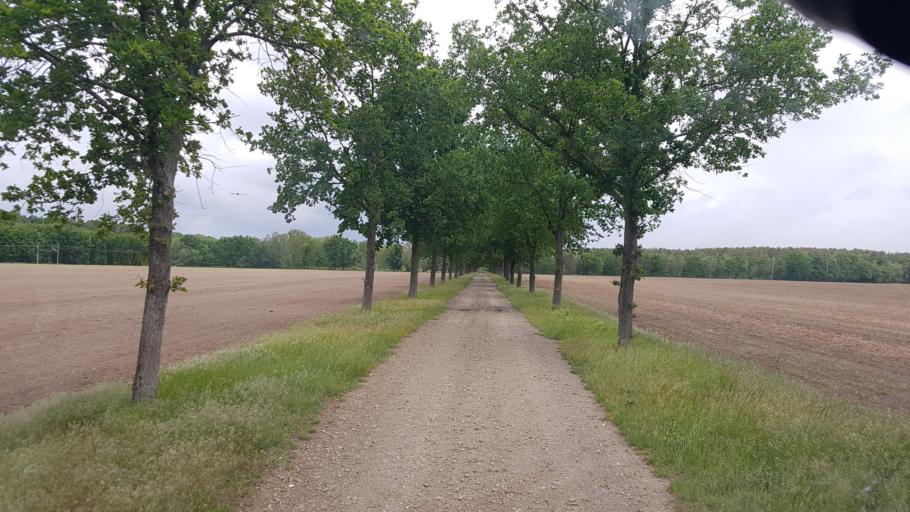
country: DE
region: Brandenburg
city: Schonewalde
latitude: 51.7083
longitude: 13.6023
